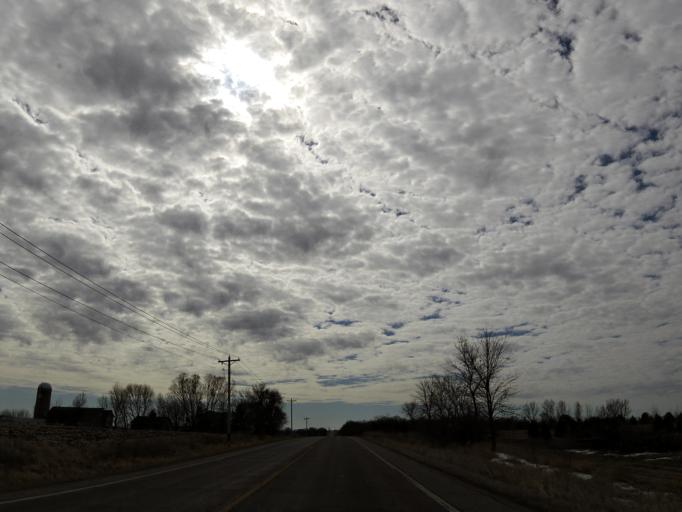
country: US
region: Minnesota
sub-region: Scott County
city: Jordan
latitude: 44.6538
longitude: -93.5625
